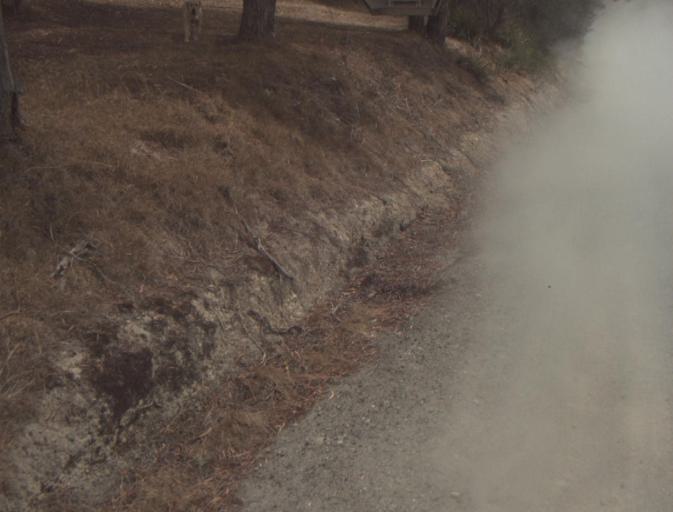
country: AU
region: Tasmania
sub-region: Launceston
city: Mayfield
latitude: -41.2061
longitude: 147.1381
